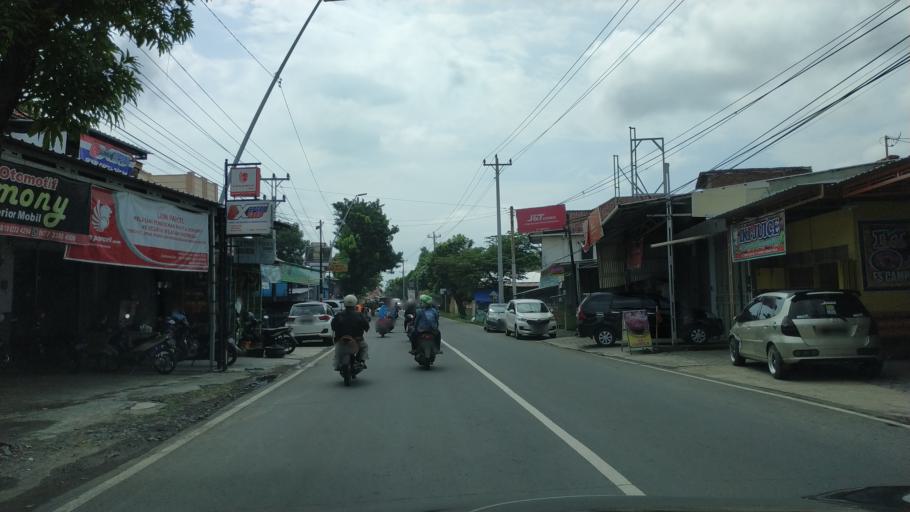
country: ID
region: Central Java
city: Tegal
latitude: -6.8918
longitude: 109.1266
